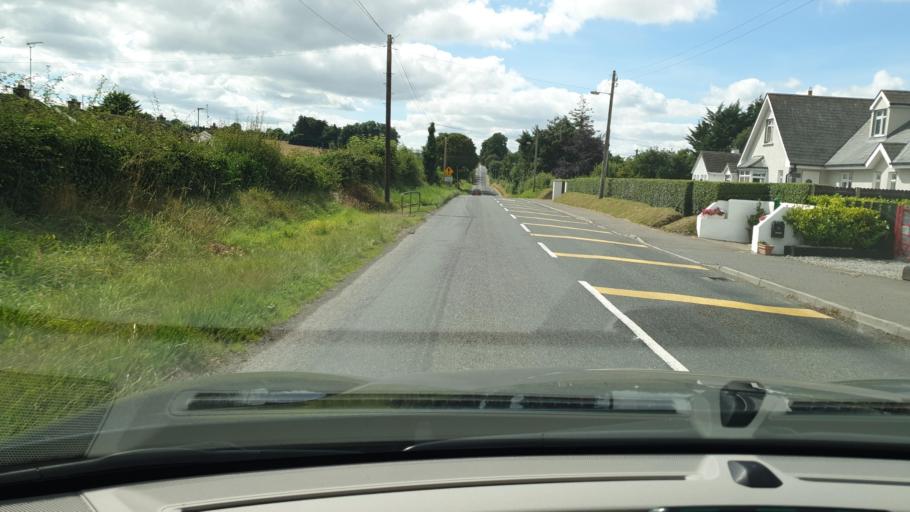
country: IE
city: Kentstown
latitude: 53.5771
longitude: -6.5496
